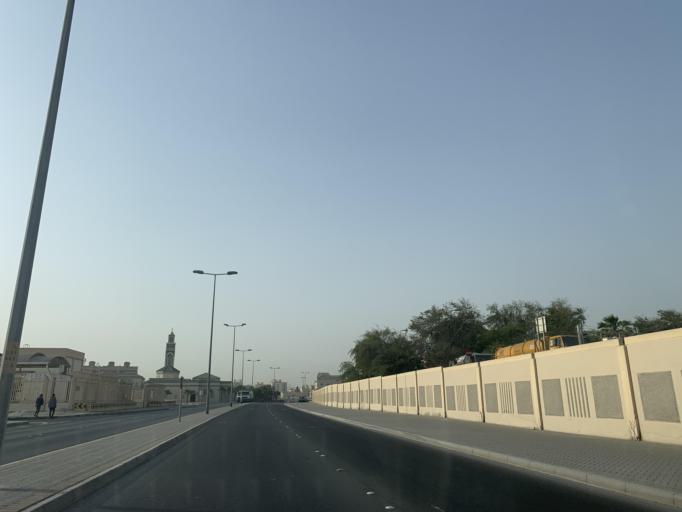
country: BH
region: Northern
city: Madinat `Isa
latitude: 26.1953
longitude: 50.5562
